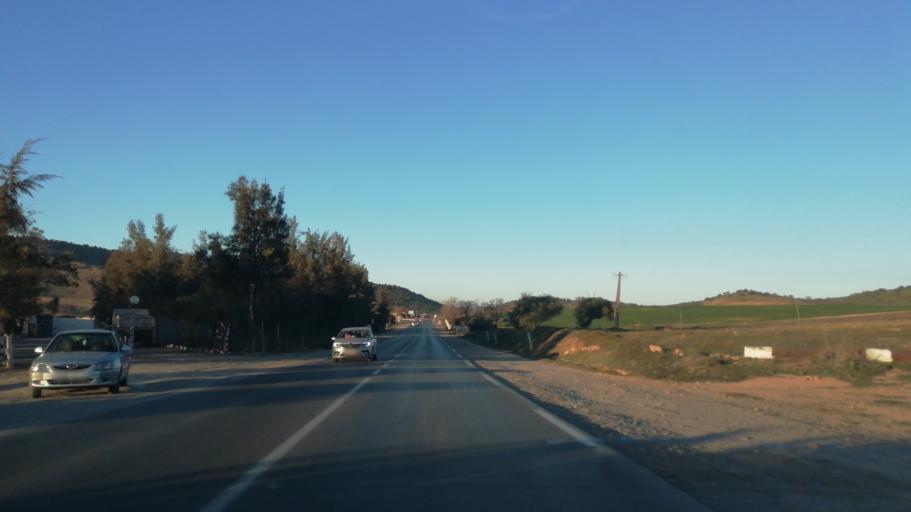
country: DZ
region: Tlemcen
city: Nedroma
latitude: 34.8588
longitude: -1.6789
